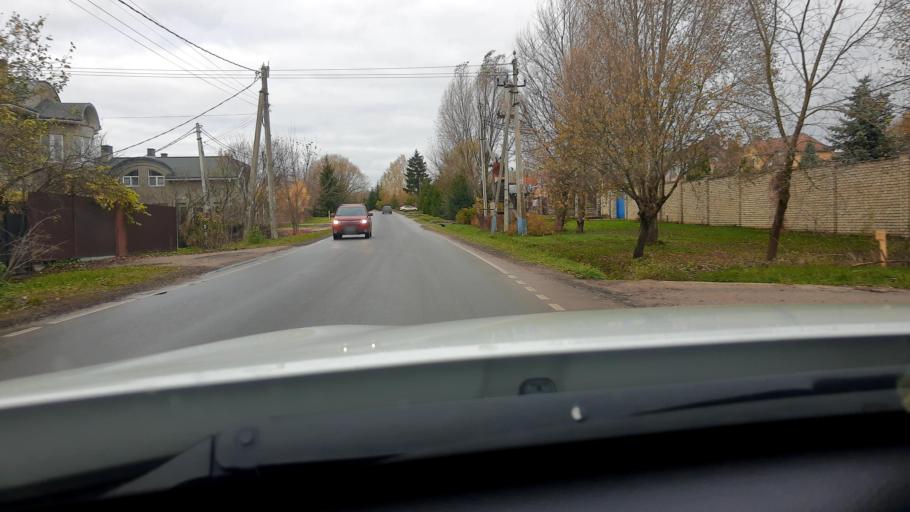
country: RU
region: Moskovskaya
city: Annino
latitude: 55.5622
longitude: 37.2374
